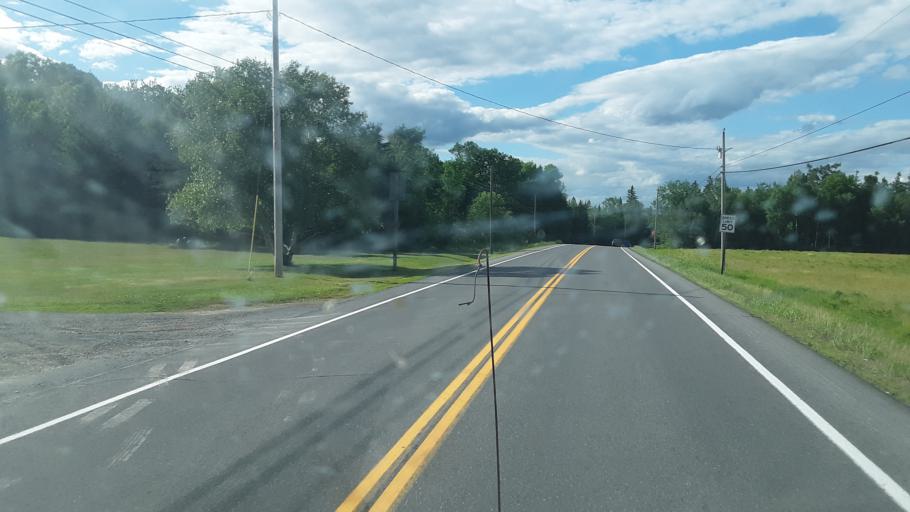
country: US
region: Maine
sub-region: Penobscot County
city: Patten
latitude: 45.9128
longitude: -68.4378
